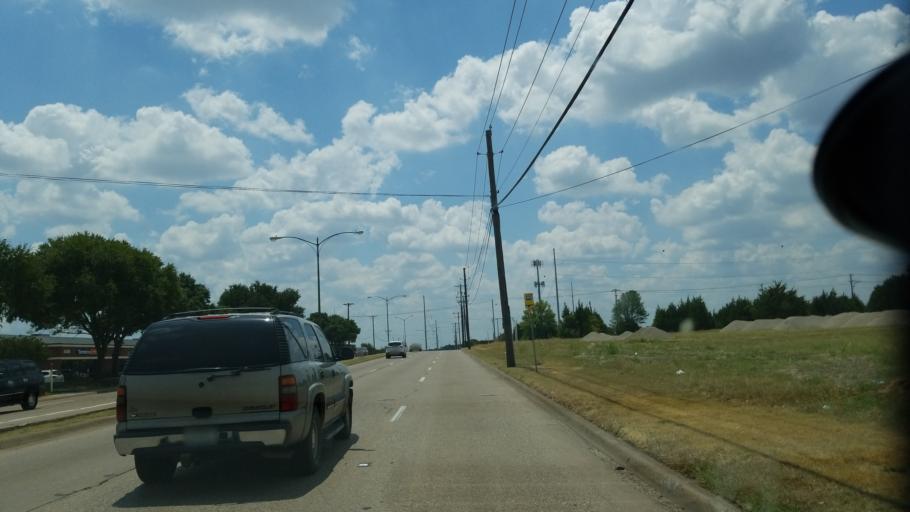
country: US
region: Texas
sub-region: Dallas County
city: Duncanville
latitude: 32.6802
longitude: -96.8829
